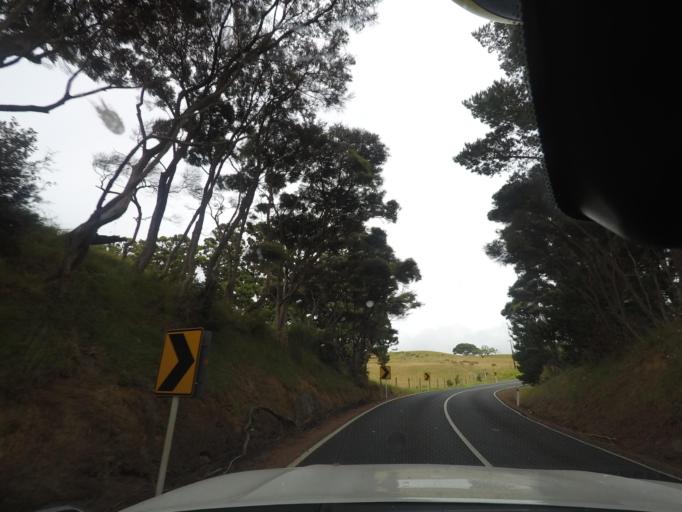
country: NZ
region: Auckland
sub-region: Auckland
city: Parakai
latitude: -36.4978
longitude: 174.2471
